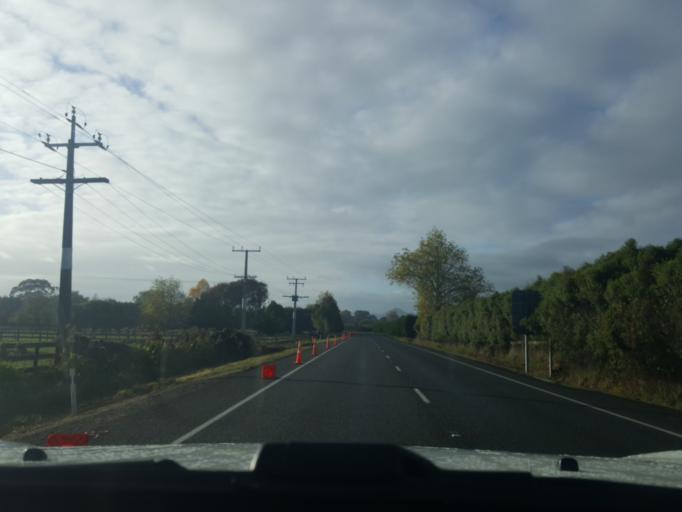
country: NZ
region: Waikato
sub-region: Hamilton City
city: Hamilton
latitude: -37.7792
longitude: 175.3894
